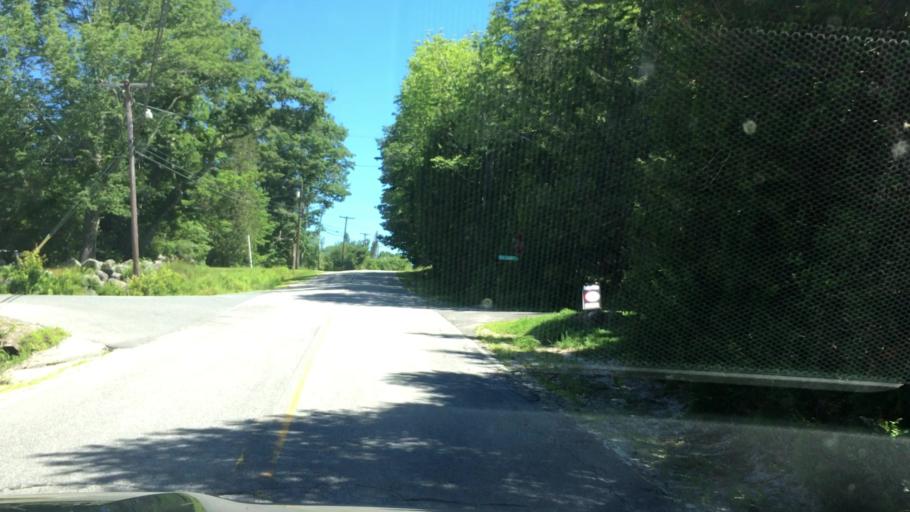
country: US
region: Maine
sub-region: Hancock County
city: Sedgwick
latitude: 44.3168
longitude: -68.6118
